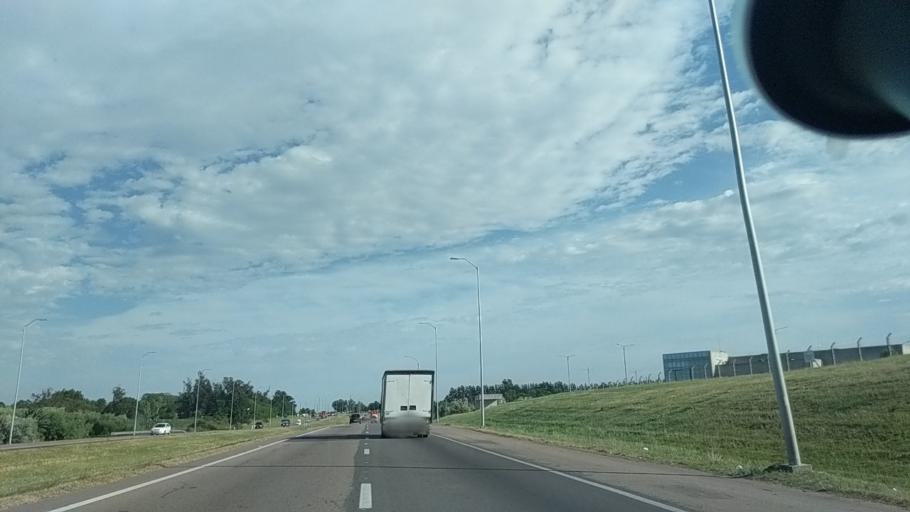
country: UY
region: Canelones
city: La Paz
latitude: -34.8067
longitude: -56.2617
